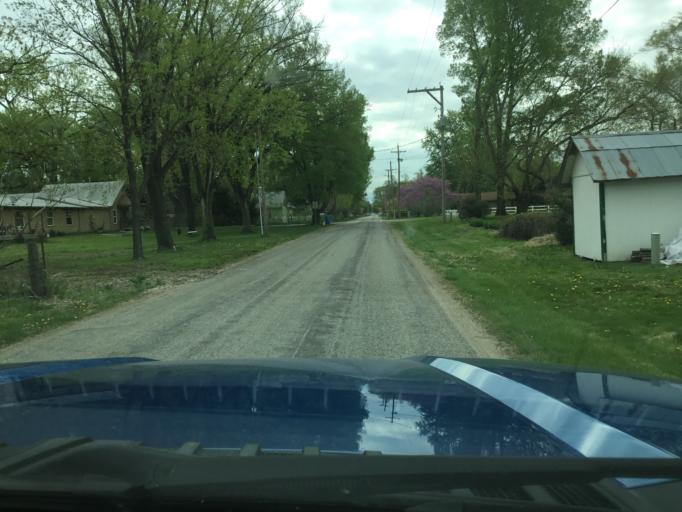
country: US
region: Kansas
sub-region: Douglas County
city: Lawrence
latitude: 38.9860
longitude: -95.2297
